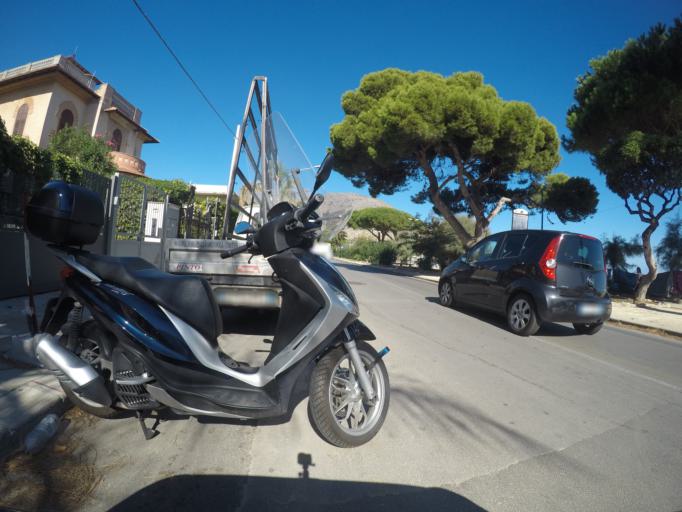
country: IT
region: Sicily
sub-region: Palermo
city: Palermo
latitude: 38.1984
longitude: 13.3298
